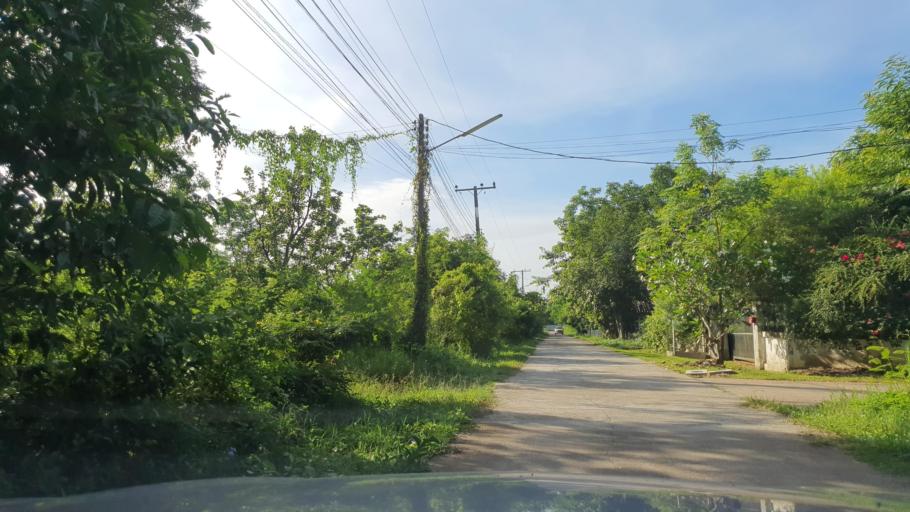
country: TH
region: Chiang Mai
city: San Kamphaeng
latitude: 18.7494
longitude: 99.1028
